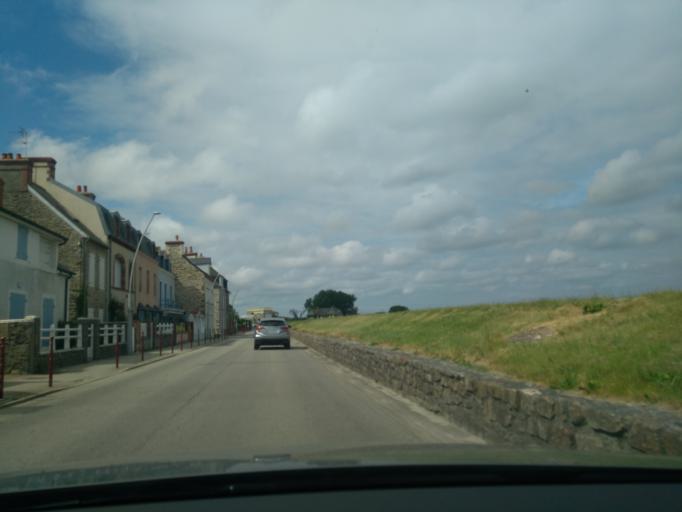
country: FR
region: Lower Normandy
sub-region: Departement de la Manche
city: Saint-Vaast-la-Hougue
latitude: 49.5908
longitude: -1.2666
